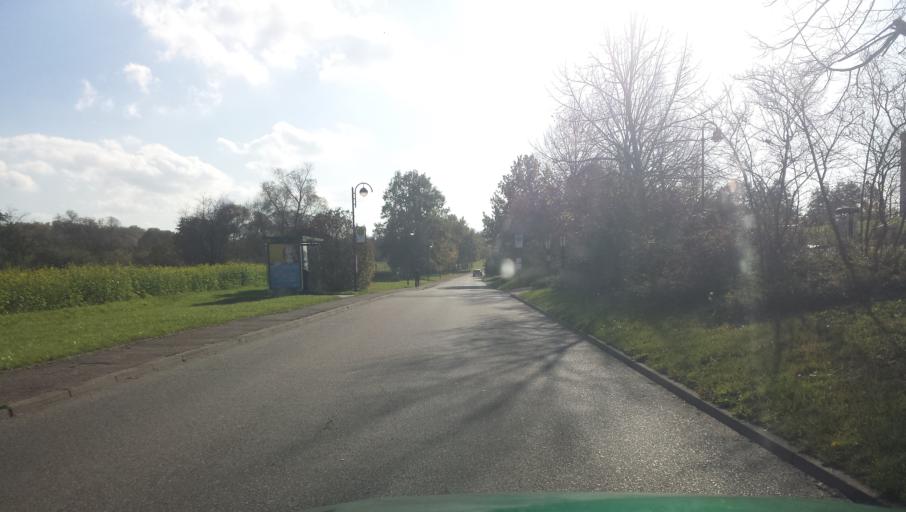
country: DE
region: Baden-Wuerttemberg
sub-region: Karlsruhe Region
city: Malsch
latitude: 49.2170
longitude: 8.6724
